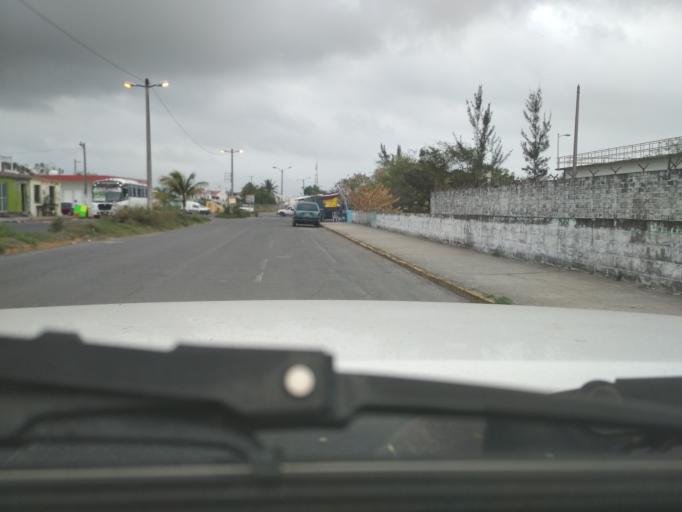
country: MX
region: Veracruz
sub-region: Veracruz
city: Fraccionamiento Geovillas los Pinos
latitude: 19.2160
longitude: -96.2246
